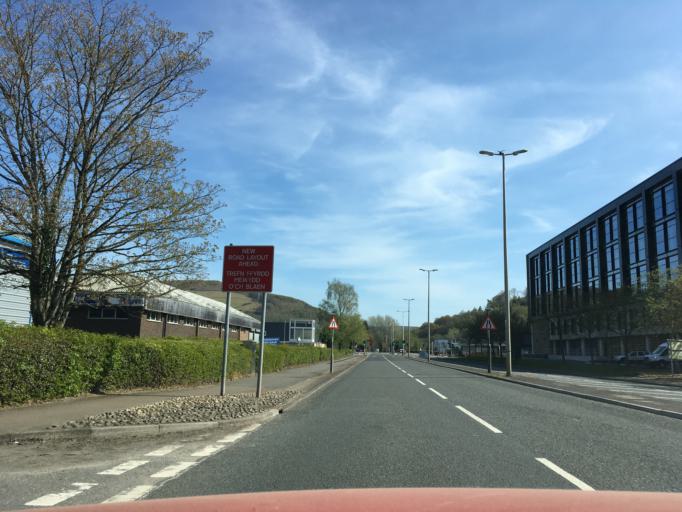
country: GB
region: Wales
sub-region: Caerphilly County Borough
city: Abertridwr
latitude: 51.5650
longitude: -3.2814
